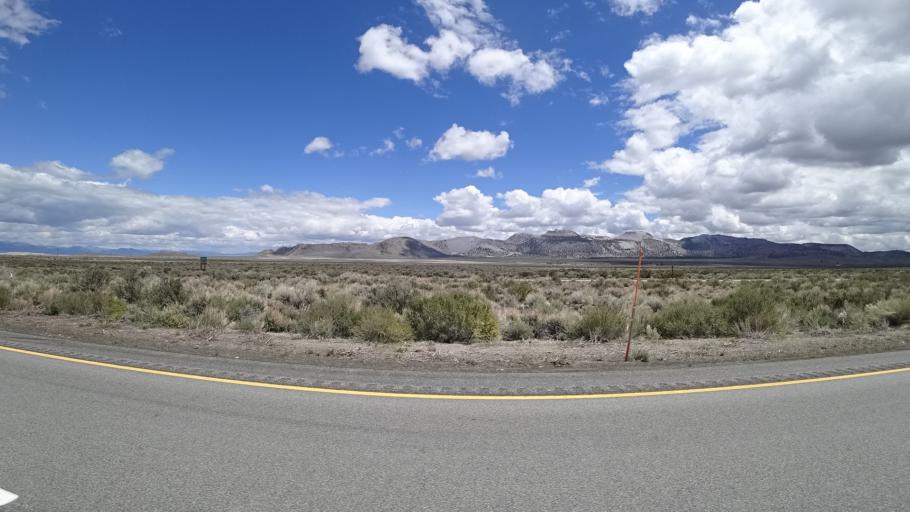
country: US
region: California
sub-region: Mono County
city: Mammoth Lakes
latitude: 37.8842
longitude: -119.0908
